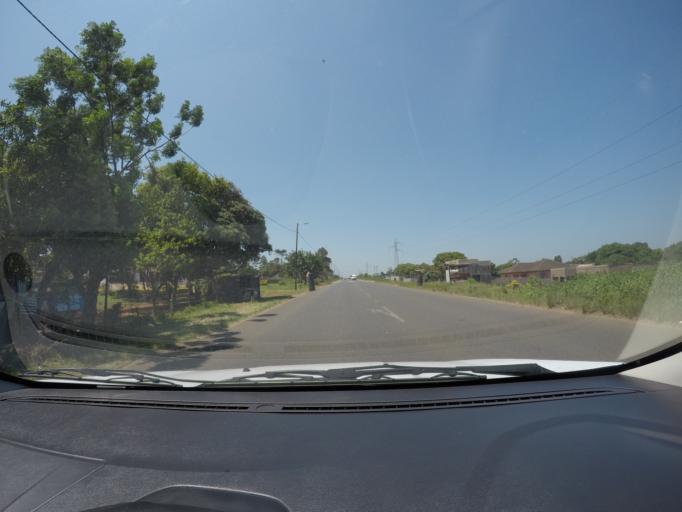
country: ZA
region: KwaZulu-Natal
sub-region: uThungulu District Municipality
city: eSikhawini
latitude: -28.8426
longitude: 31.9341
